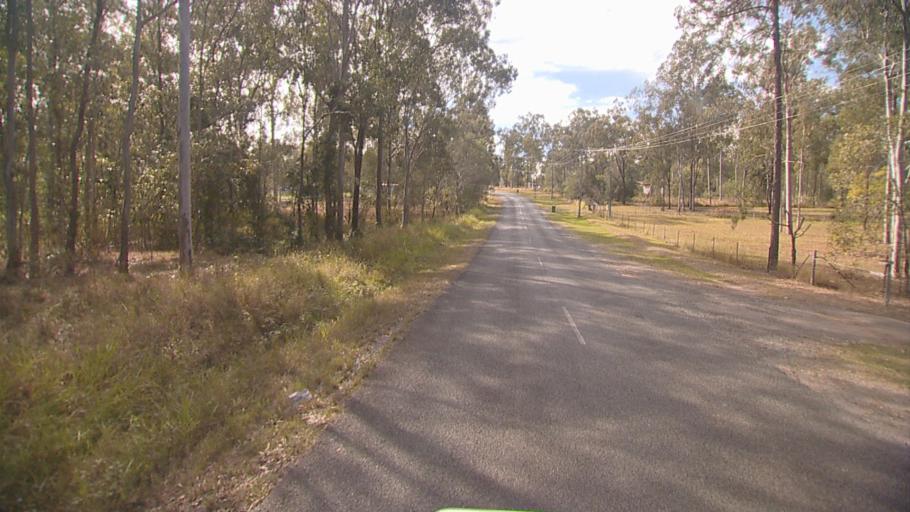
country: AU
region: Queensland
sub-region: Logan
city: North Maclean
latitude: -27.7398
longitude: 152.9775
